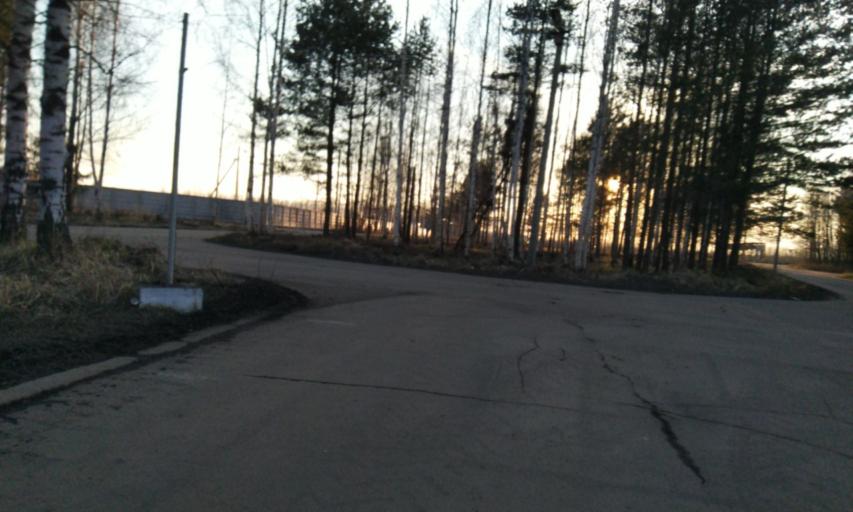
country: RU
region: Leningrad
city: Novoye Devyatkino
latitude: 60.0763
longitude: 30.4696
